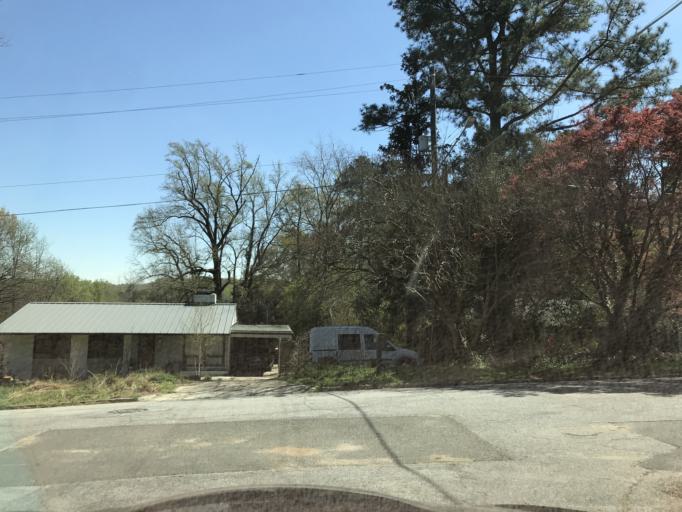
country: US
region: North Carolina
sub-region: Wake County
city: West Raleigh
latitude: 35.7693
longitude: -78.6964
